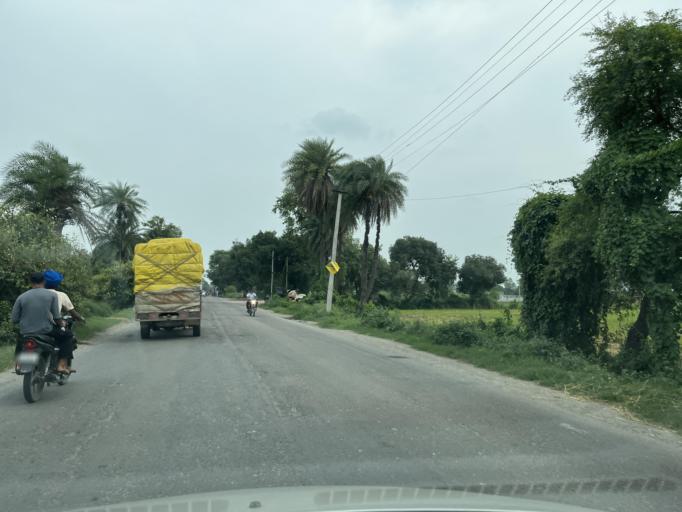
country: IN
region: Uttar Pradesh
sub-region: Rampur
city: Bilaspur
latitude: 29.0342
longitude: 79.2583
